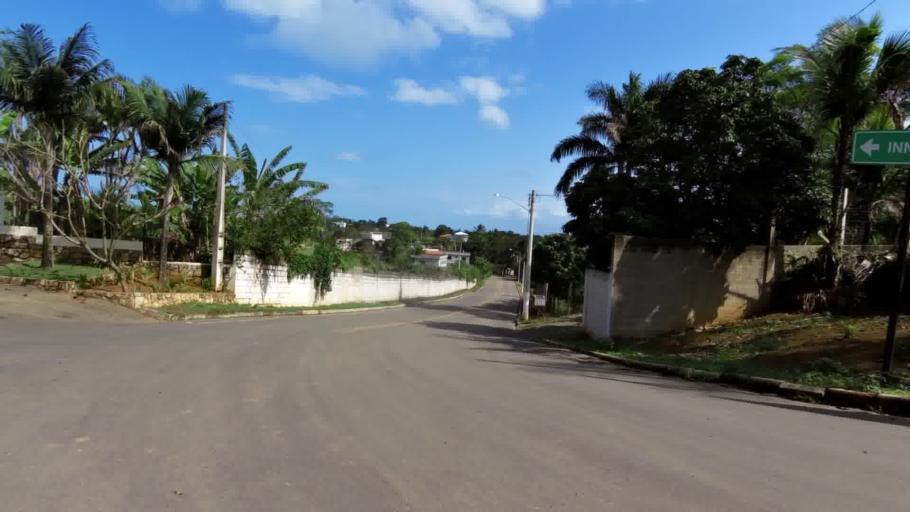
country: BR
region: Espirito Santo
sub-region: Piuma
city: Piuma
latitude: -20.8183
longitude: -40.6810
